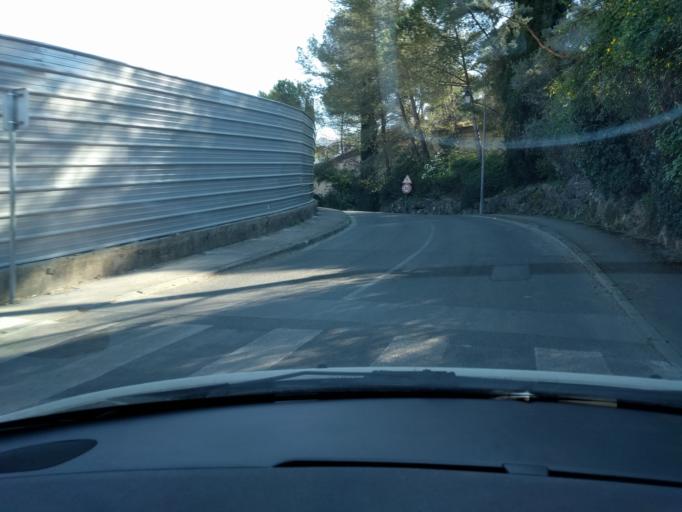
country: FR
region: Provence-Alpes-Cote d'Azur
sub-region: Departement des Alpes-Maritimes
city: Mougins
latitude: 43.6005
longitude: 6.9863
